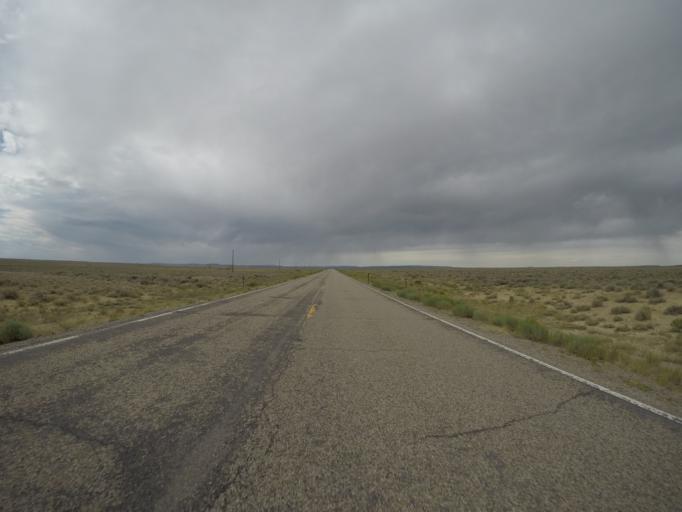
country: US
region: Wyoming
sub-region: Lincoln County
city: Kemmerer
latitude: 41.9628
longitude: -110.1170
